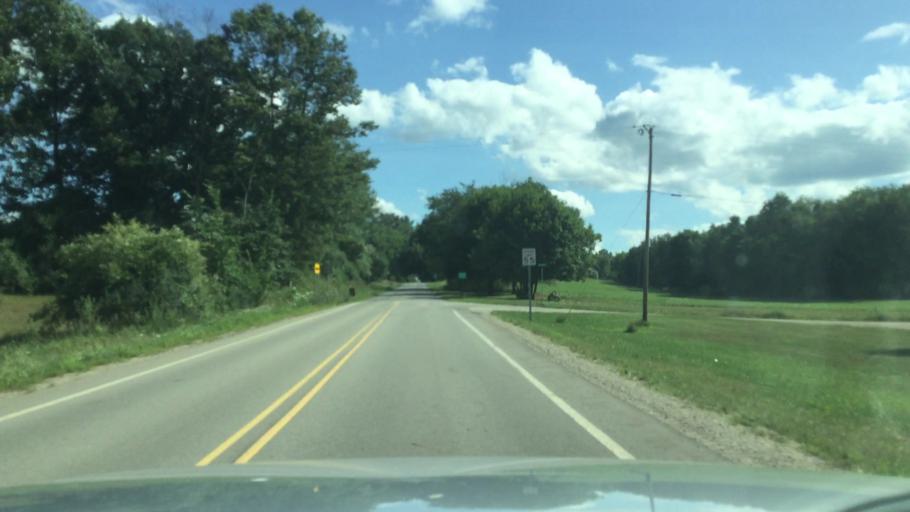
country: US
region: Michigan
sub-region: Ionia County
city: Belding
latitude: 43.0786
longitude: -85.2282
